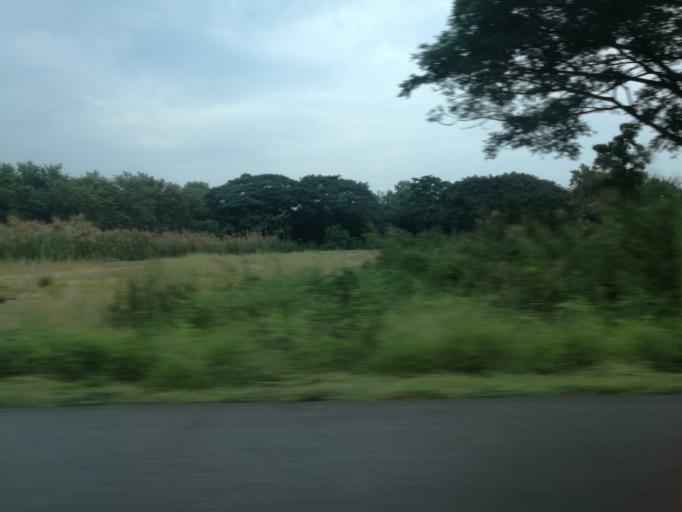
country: TH
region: Prachuap Khiri Khan
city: Kui Buri
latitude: 12.0893
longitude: 99.8540
